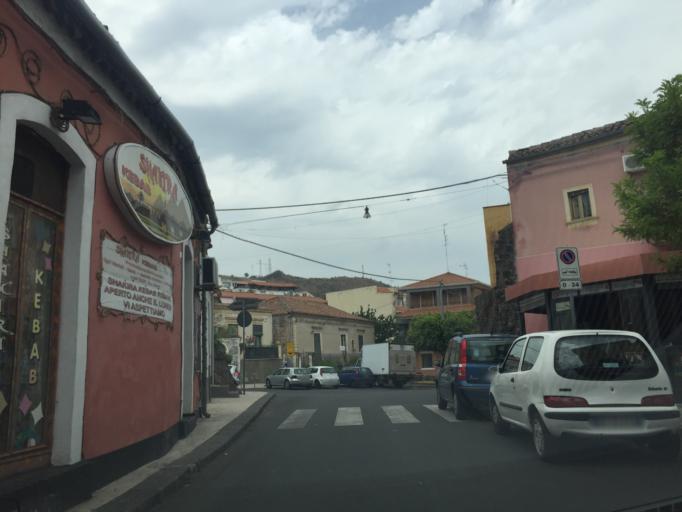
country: IT
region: Sicily
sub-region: Catania
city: Aci Castello
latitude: 37.5562
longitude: 15.1468
